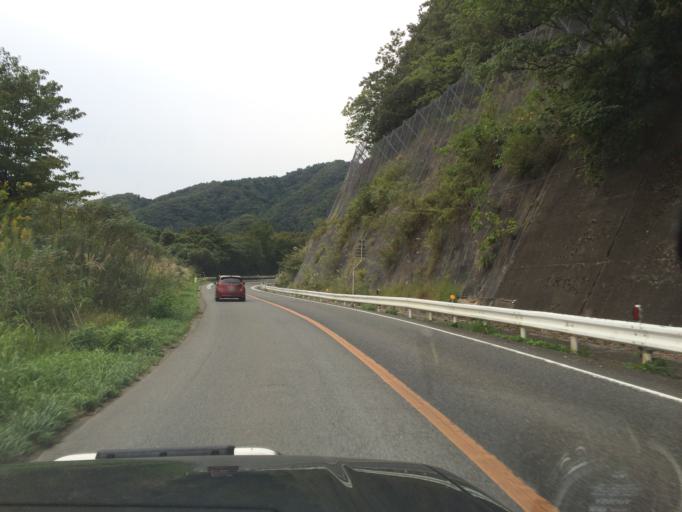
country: JP
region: Hyogo
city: Toyooka
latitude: 35.4061
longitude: 134.7822
